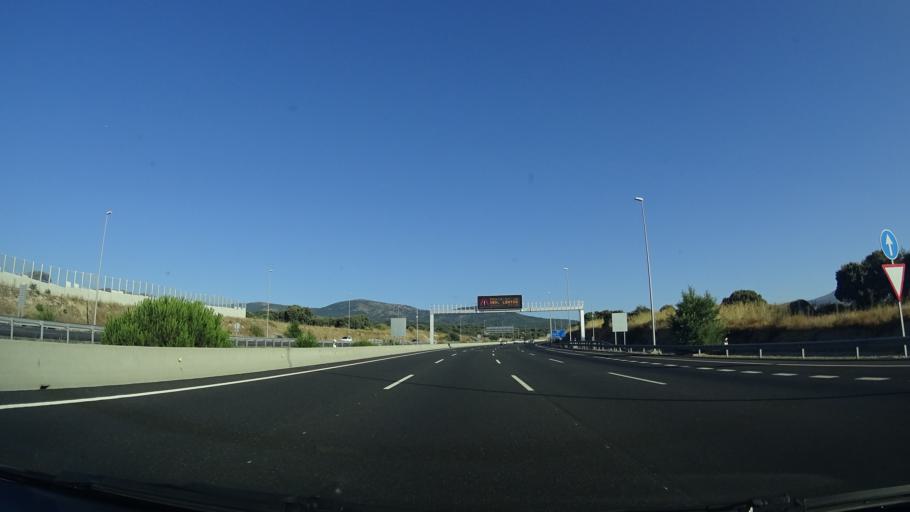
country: ES
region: Madrid
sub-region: Provincia de Madrid
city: Guadarrama
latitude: 40.6583
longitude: -4.0954
